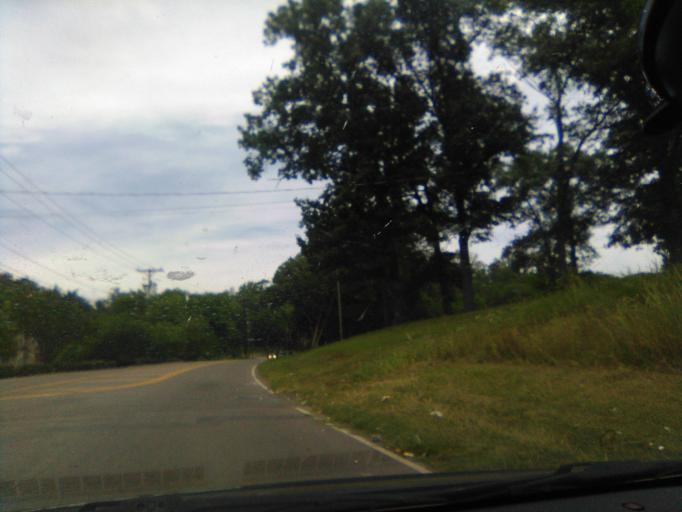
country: US
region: Tennessee
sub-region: Davidson County
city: Belle Meade
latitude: 36.1289
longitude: -86.9102
